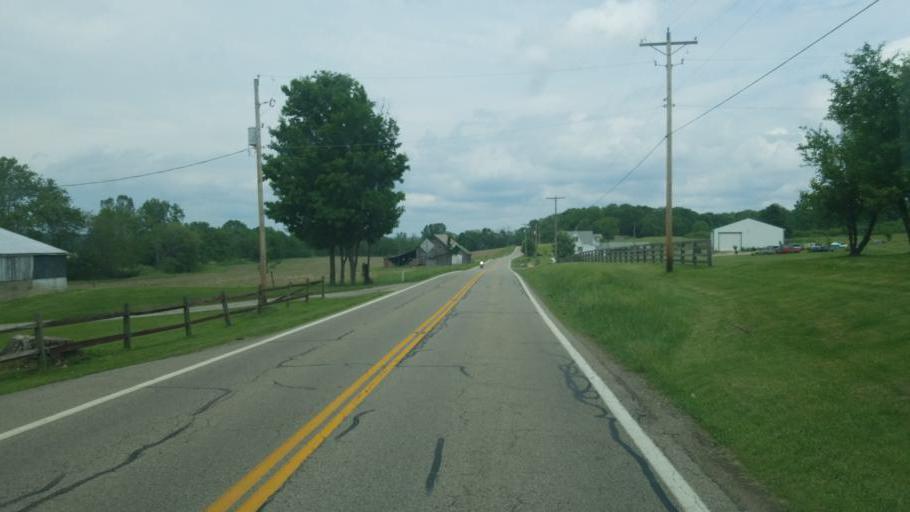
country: US
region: Ohio
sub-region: Perry County
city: Thornport
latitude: 39.9012
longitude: -82.3857
